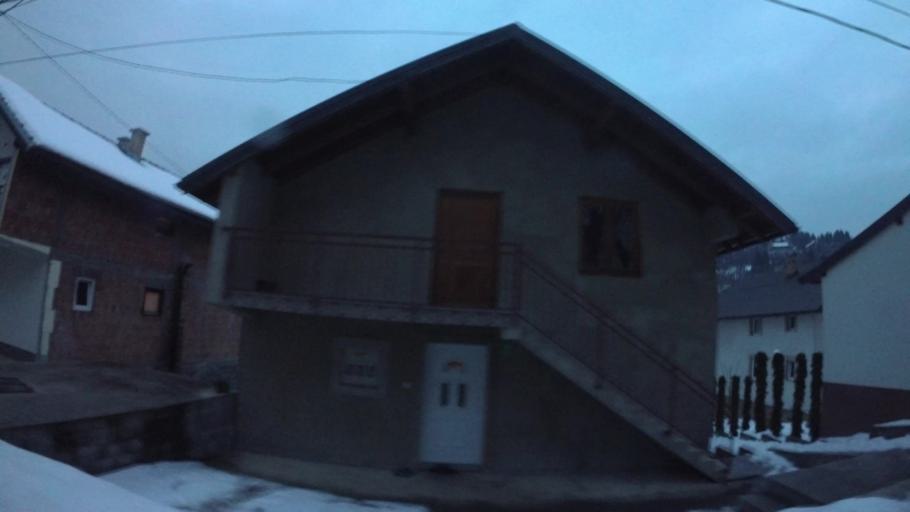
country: BA
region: Federation of Bosnia and Herzegovina
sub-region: Kanton Sarajevo
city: Sarajevo
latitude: 43.8547
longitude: 18.3410
